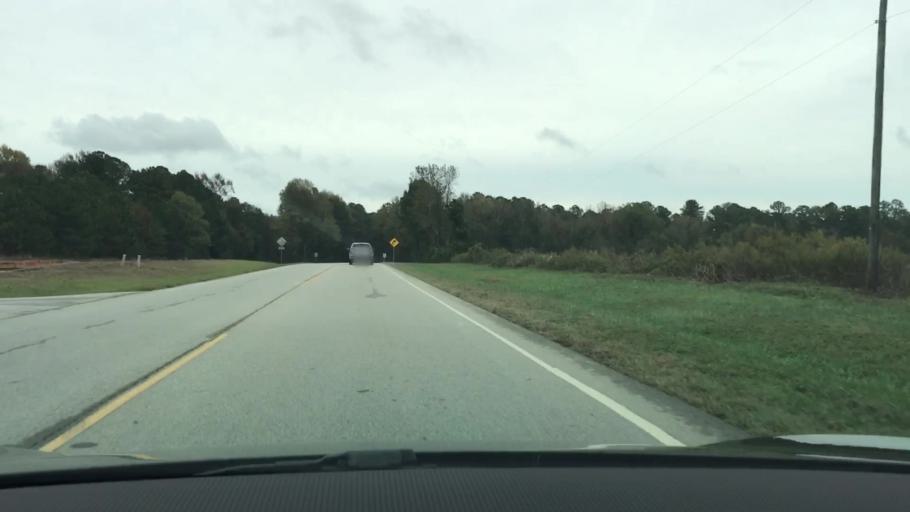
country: US
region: Georgia
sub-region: Warren County
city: Firing Range
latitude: 33.4683
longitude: -82.7165
